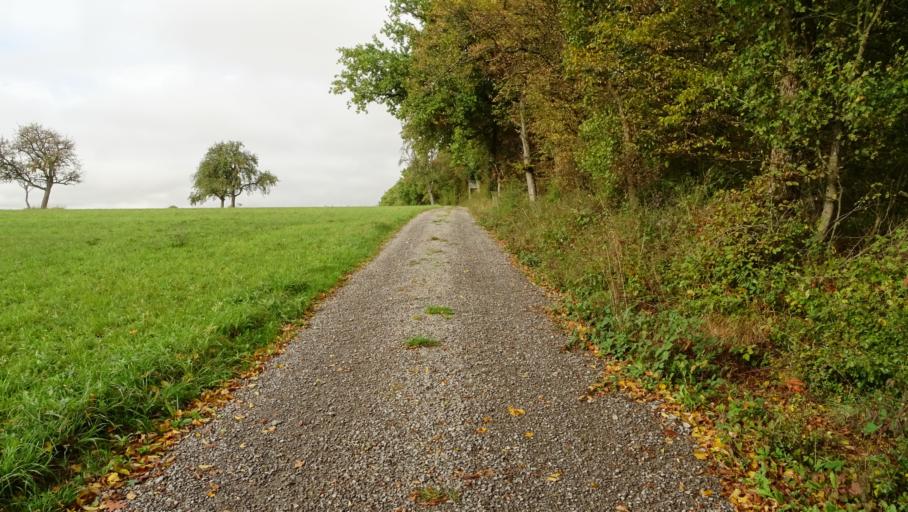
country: DE
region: Baden-Wuerttemberg
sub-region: Karlsruhe Region
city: Obrigheim
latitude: 49.3879
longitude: 9.1062
